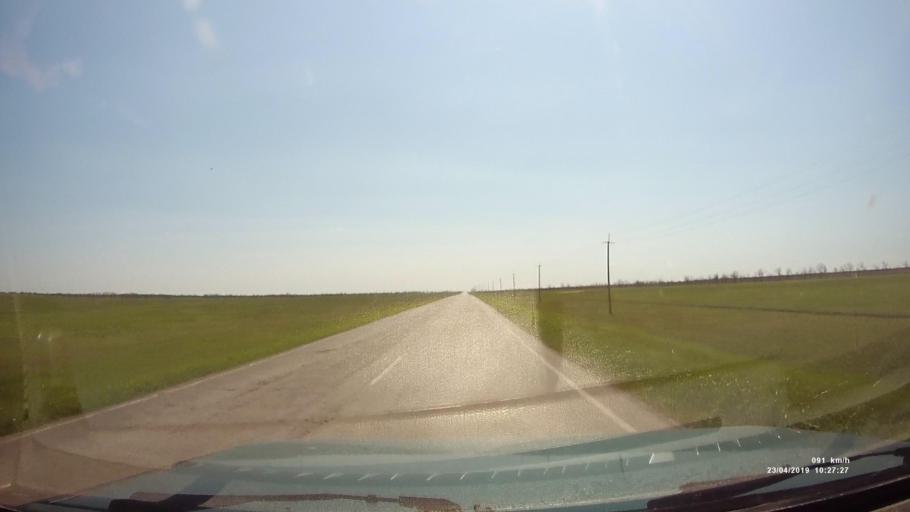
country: RU
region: Kalmykiya
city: Yashalta
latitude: 46.6137
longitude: 42.4912
